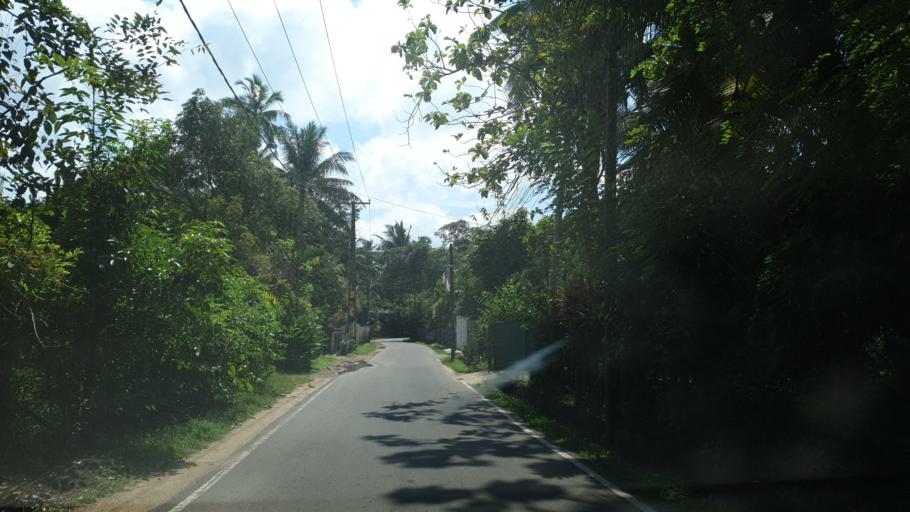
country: LK
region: Western
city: Panadura
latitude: 6.6856
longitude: 79.9301
